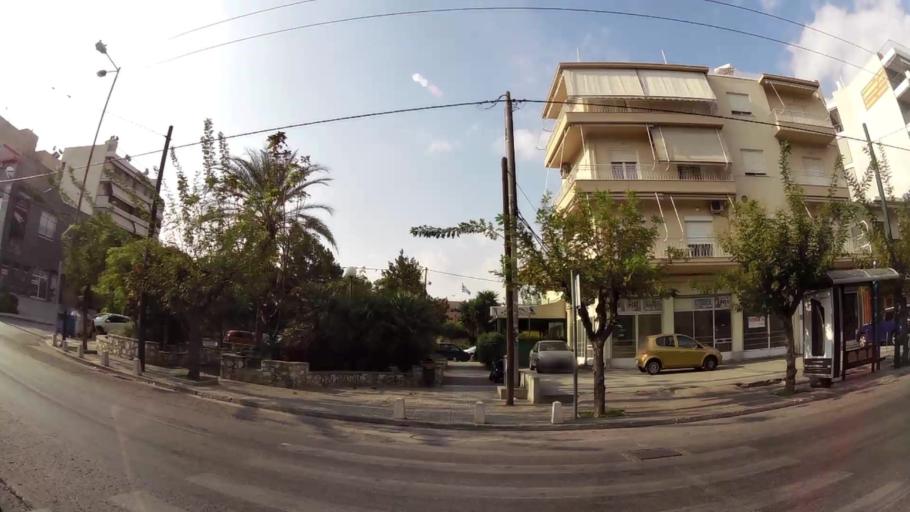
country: GR
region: Attica
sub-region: Nomarchia Athinas
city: Moskhaton
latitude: 37.9466
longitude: 23.6873
